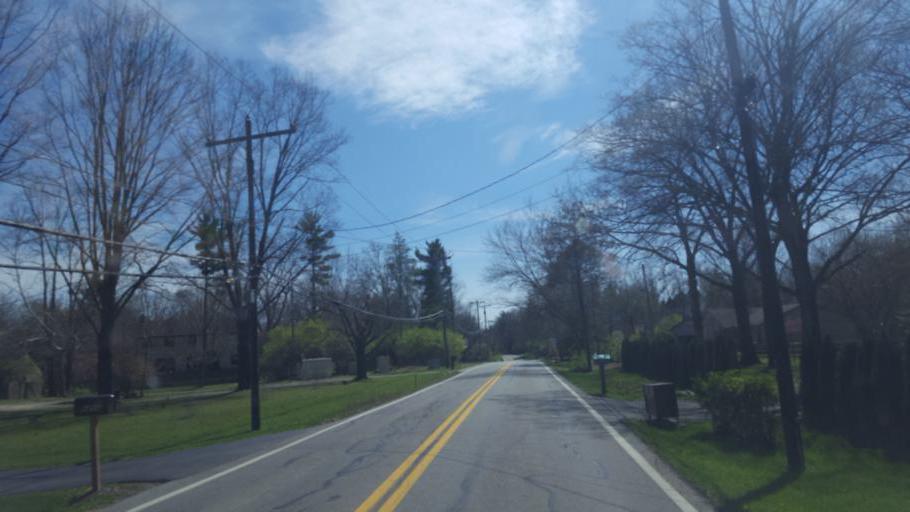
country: US
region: Ohio
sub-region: Franklin County
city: Worthington
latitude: 40.0973
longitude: -83.0485
